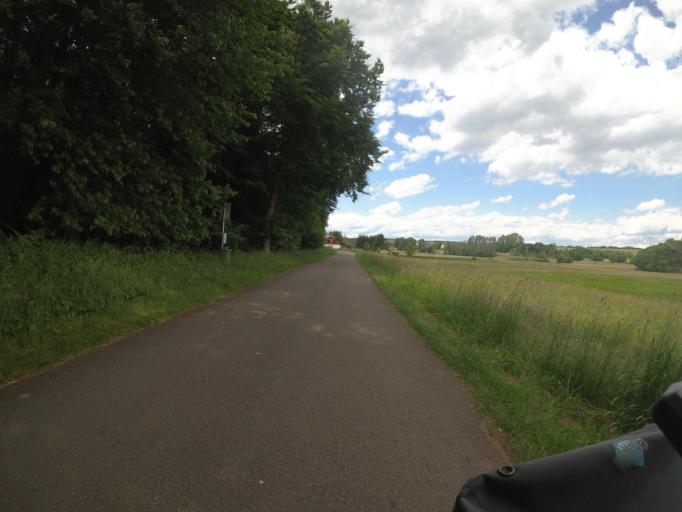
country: DE
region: Rheinland-Pfalz
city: Bruchmuhlbach-Miesau
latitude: 49.4162
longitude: 7.4392
